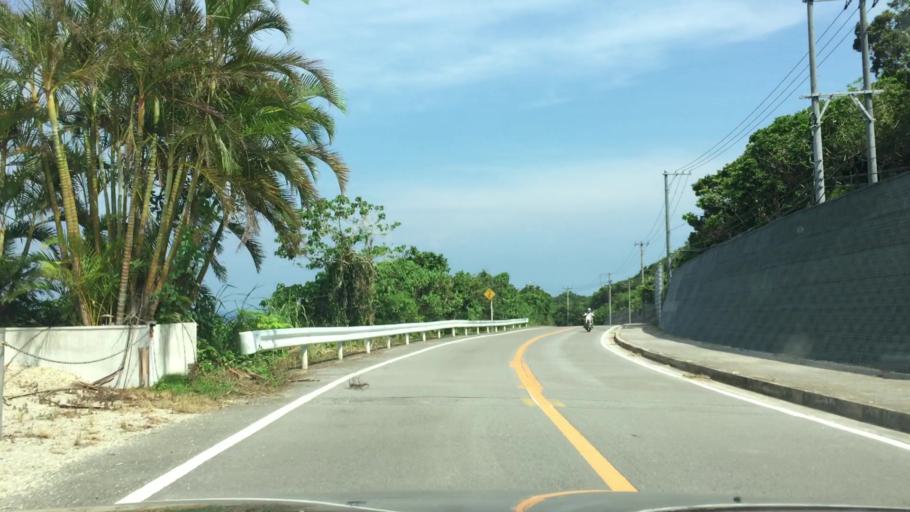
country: JP
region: Okinawa
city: Ishigaki
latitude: 24.5159
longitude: 124.2620
